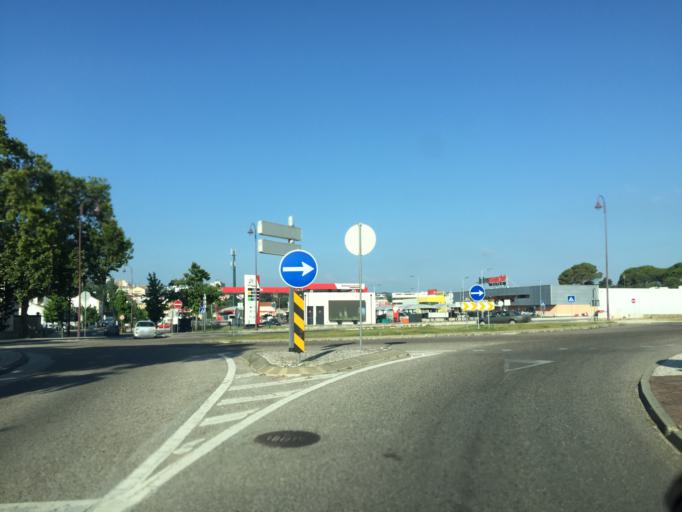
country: PT
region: Santarem
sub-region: Abrantes
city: Abrantes
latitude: 39.4750
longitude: -8.1905
